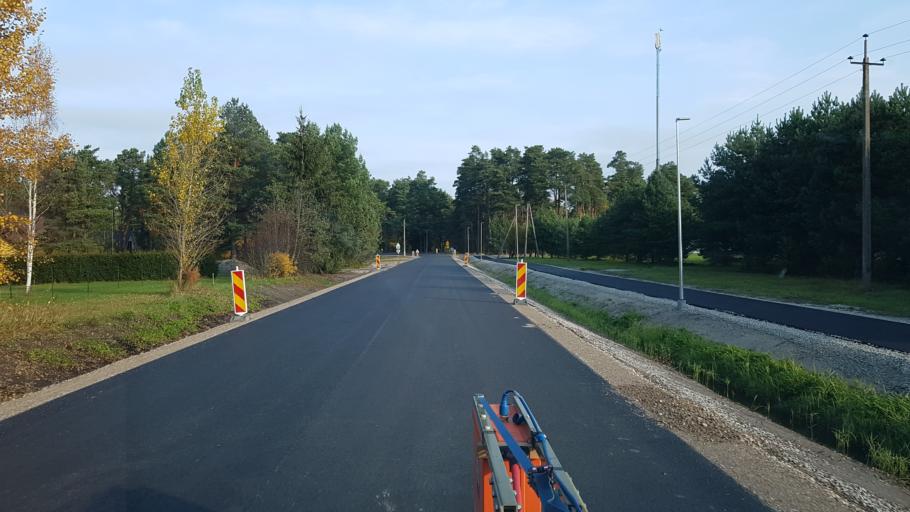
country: EE
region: Paernumaa
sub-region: Paikuse vald
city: Paikuse
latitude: 58.3454
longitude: 24.6212
